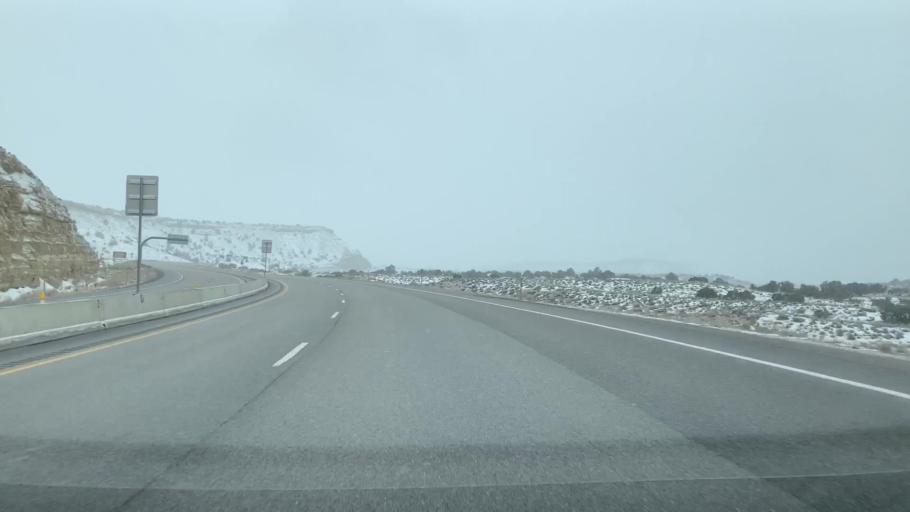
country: US
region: Utah
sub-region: Emery County
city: Castle Dale
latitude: 38.9366
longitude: -110.4869
